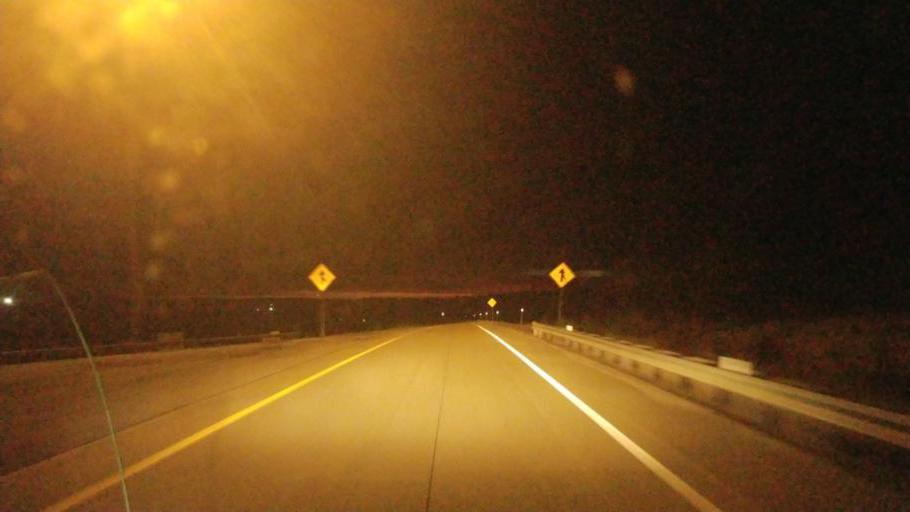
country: US
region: Missouri
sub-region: Howell County
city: Willow Springs
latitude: 36.9639
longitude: -91.9276
